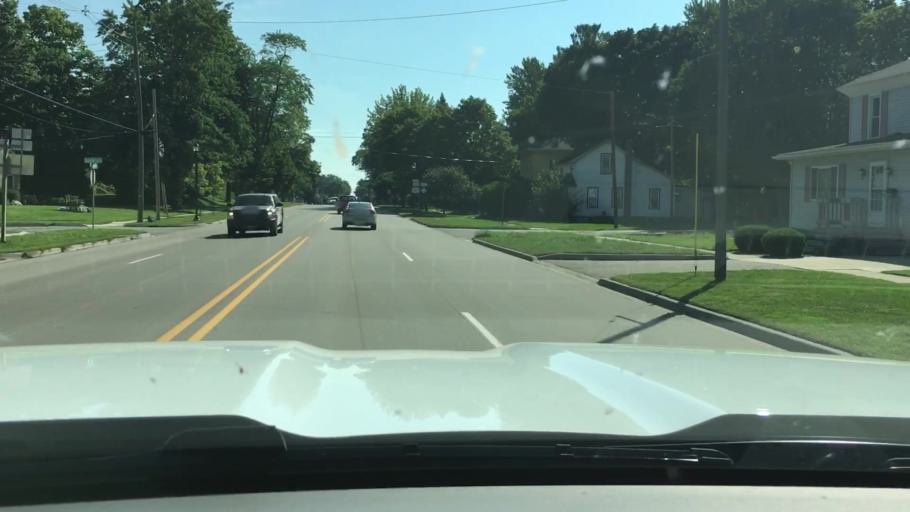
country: US
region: Michigan
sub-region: Gratiot County
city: Saint Louis
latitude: 43.4079
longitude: -84.6143
